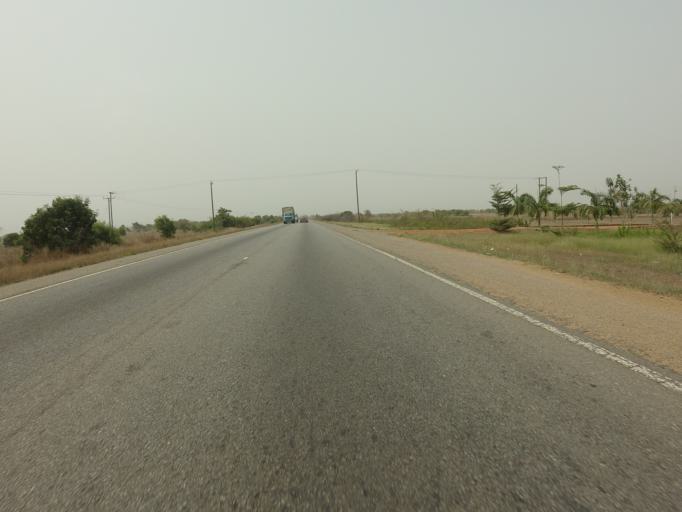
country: GH
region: Greater Accra
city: Tema
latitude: 5.8710
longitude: 0.3296
